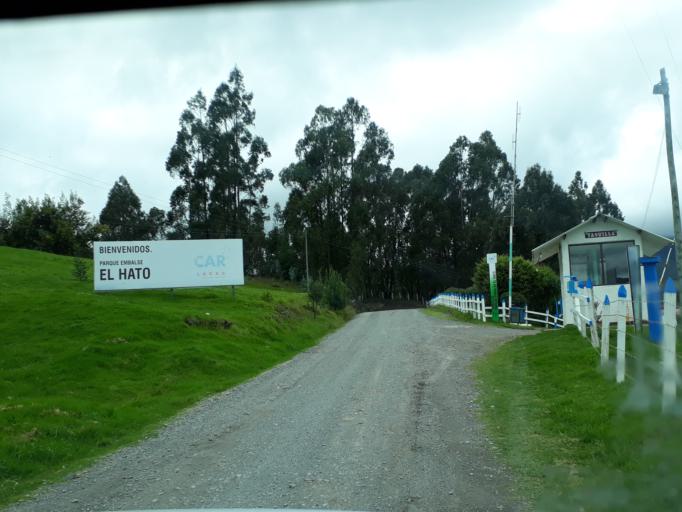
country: CO
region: Cundinamarca
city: La Mesa
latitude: 5.2923
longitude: -73.9062
